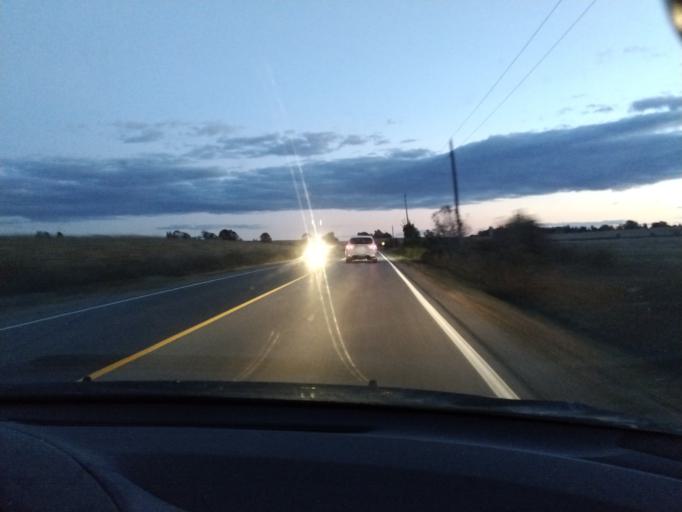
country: CA
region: Ontario
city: Bradford West Gwillimbury
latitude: 44.1079
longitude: -79.6418
